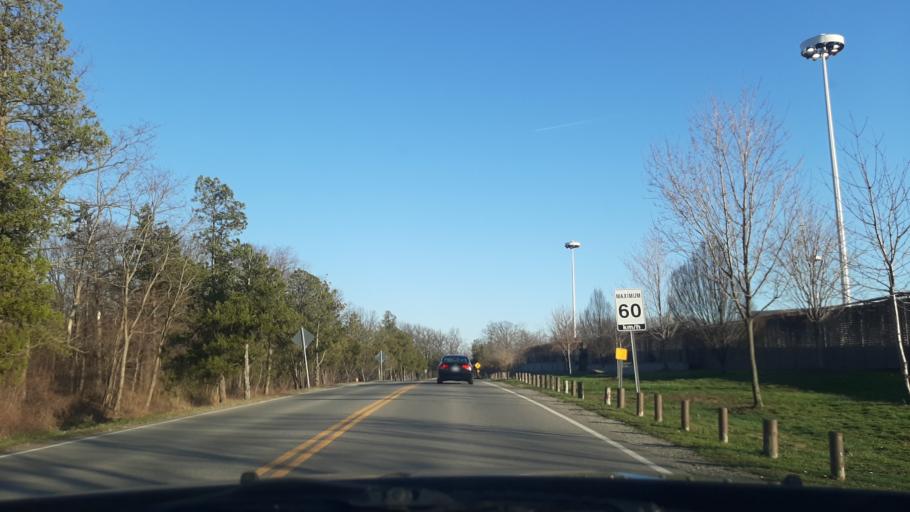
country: US
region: New York
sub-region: Niagara County
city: Lewiston
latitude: 43.1573
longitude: -79.0496
